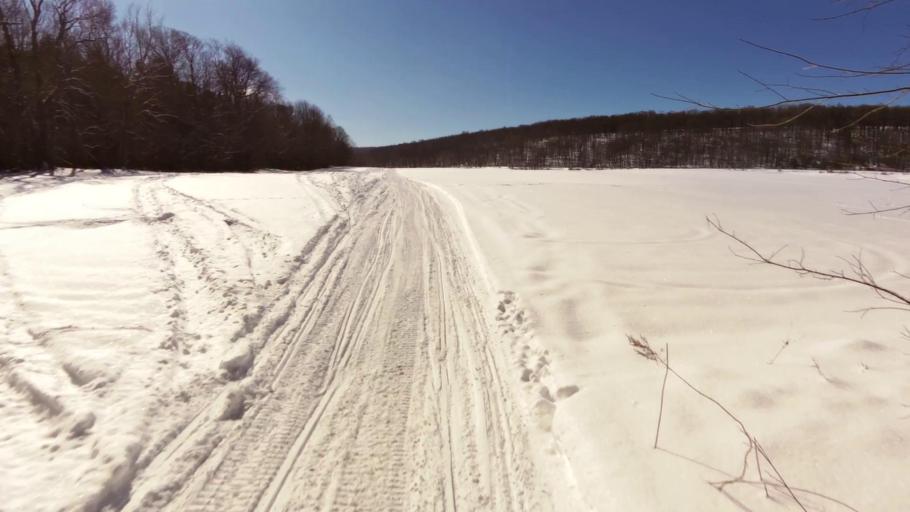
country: US
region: New York
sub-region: Chautauqua County
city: Fredonia
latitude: 42.3583
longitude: -79.1788
